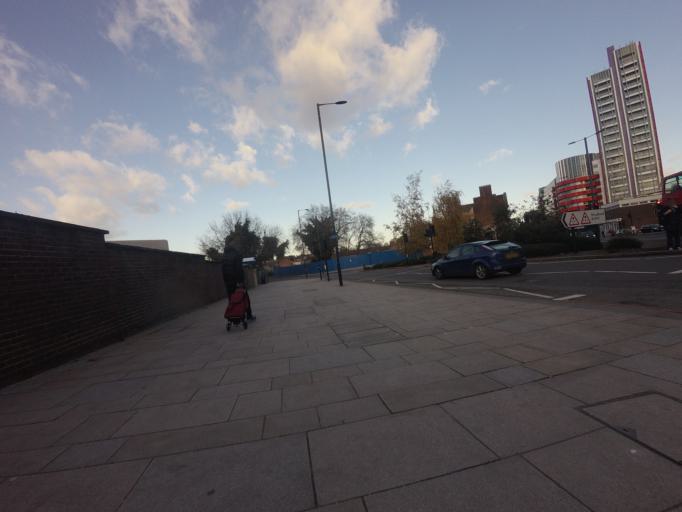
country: GB
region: England
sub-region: Greater London
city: Poplar
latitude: 51.5158
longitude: 0.0074
